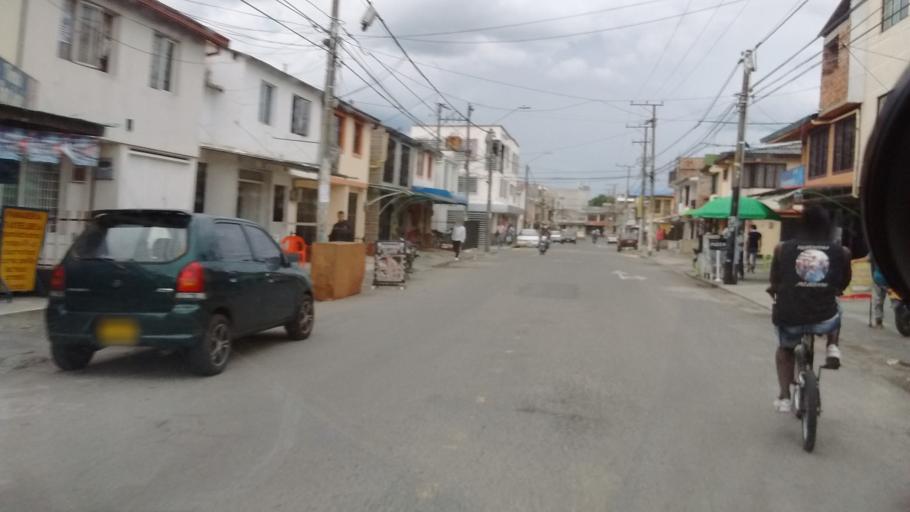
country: CO
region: Cauca
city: Popayan
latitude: 2.4421
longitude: -76.6187
